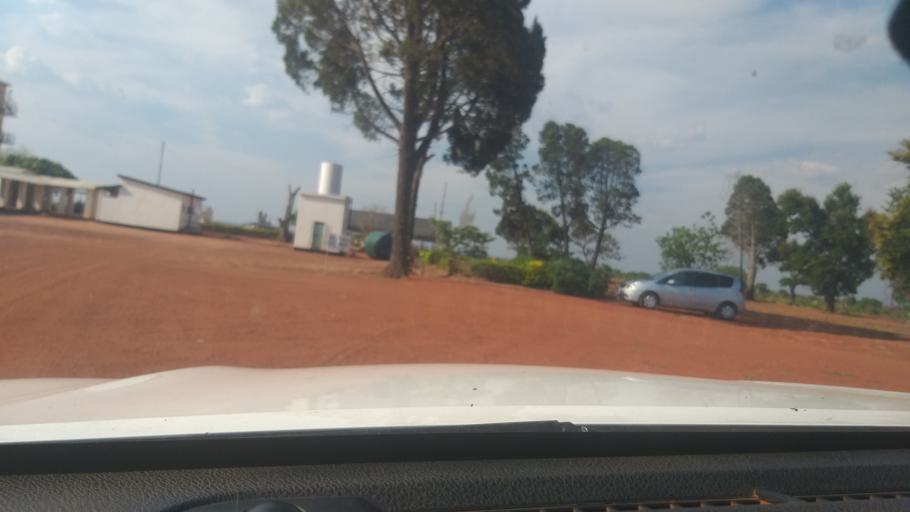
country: ZM
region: Northern
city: Kasama
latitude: -10.2176
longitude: 31.1361
